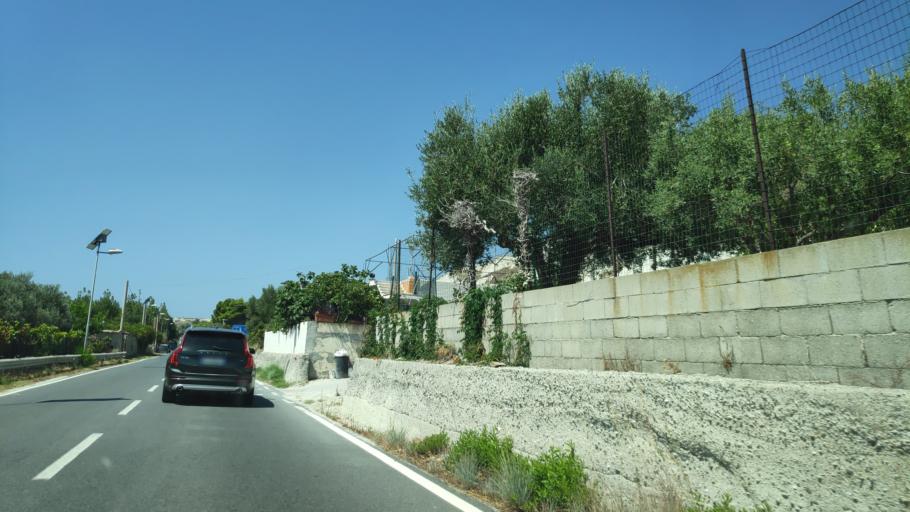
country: IT
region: Calabria
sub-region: Provincia di Reggio Calabria
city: Palizzi Marina
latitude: 37.9232
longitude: 16.0197
